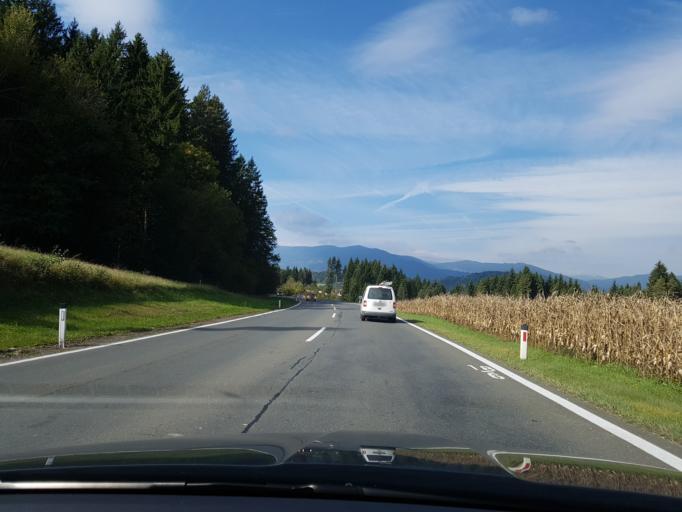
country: AT
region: Carinthia
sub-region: Politischer Bezirk Feldkirchen
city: Feldkirchen in Karnten
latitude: 46.6921
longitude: 14.1349
